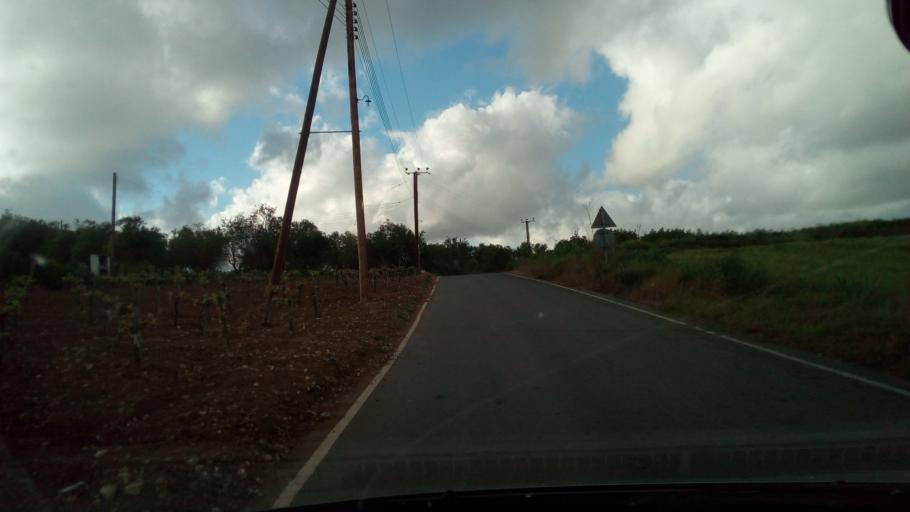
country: CY
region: Pafos
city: Mesogi
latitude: 34.8767
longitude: 32.5052
